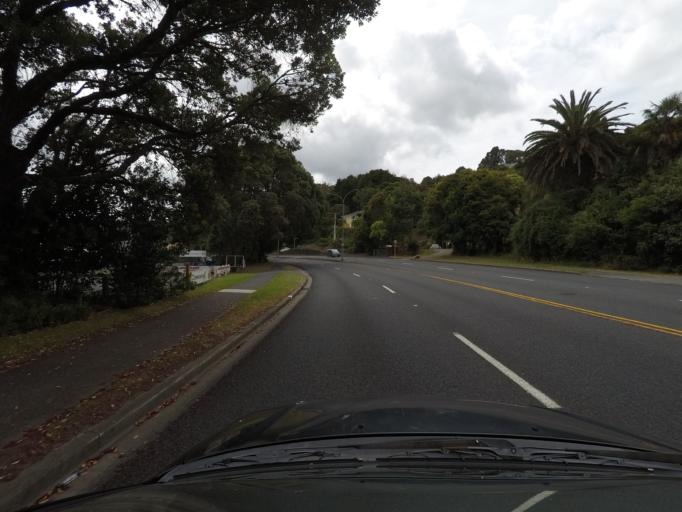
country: NZ
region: Northland
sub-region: Whangarei
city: Whangarei
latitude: -35.7255
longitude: 174.3314
